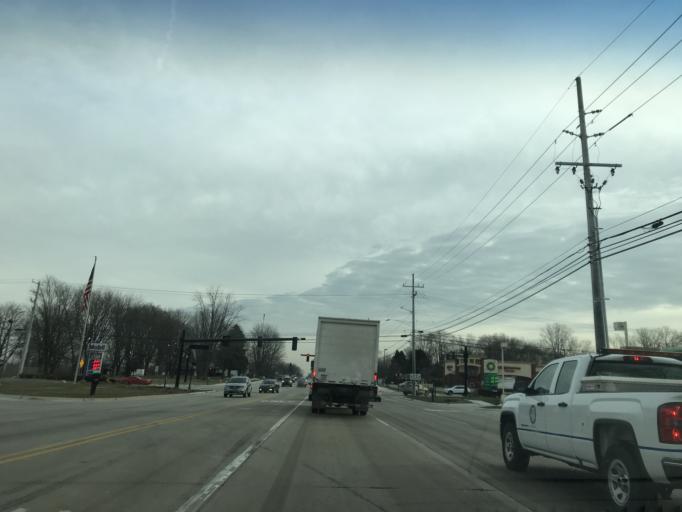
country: US
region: Michigan
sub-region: Macomb County
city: Mount Clemens
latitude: 42.6733
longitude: -82.8793
